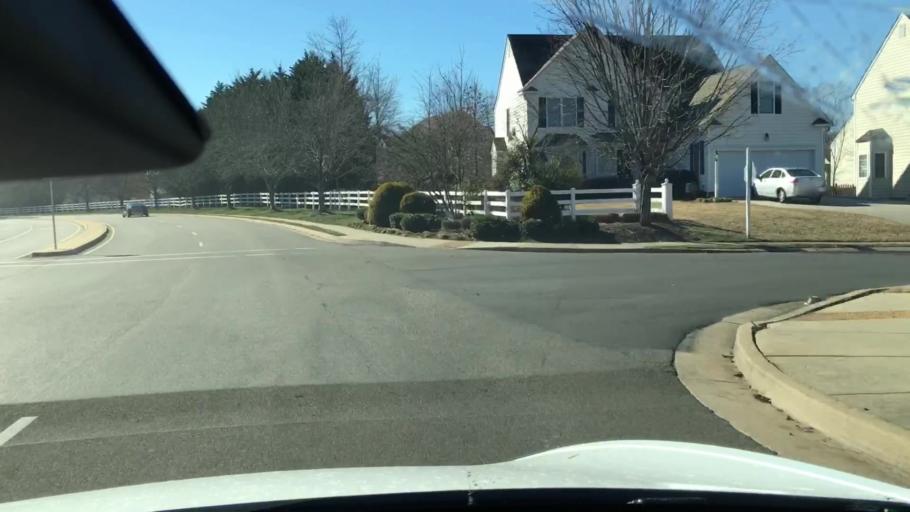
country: US
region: Virginia
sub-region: Henrico County
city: Glen Allen
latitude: 37.6698
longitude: -77.4664
